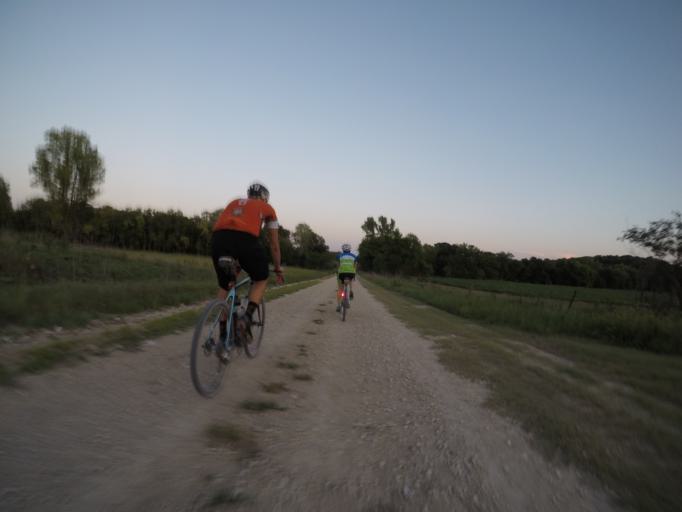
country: US
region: Kansas
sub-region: Riley County
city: Ogden
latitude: 38.9915
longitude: -96.5644
